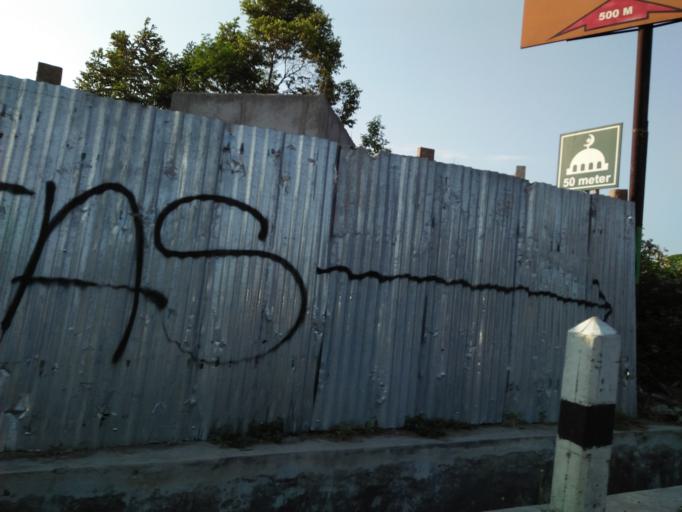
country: ID
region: Daerah Istimewa Yogyakarta
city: Depok
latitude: -7.7777
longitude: 110.4578
